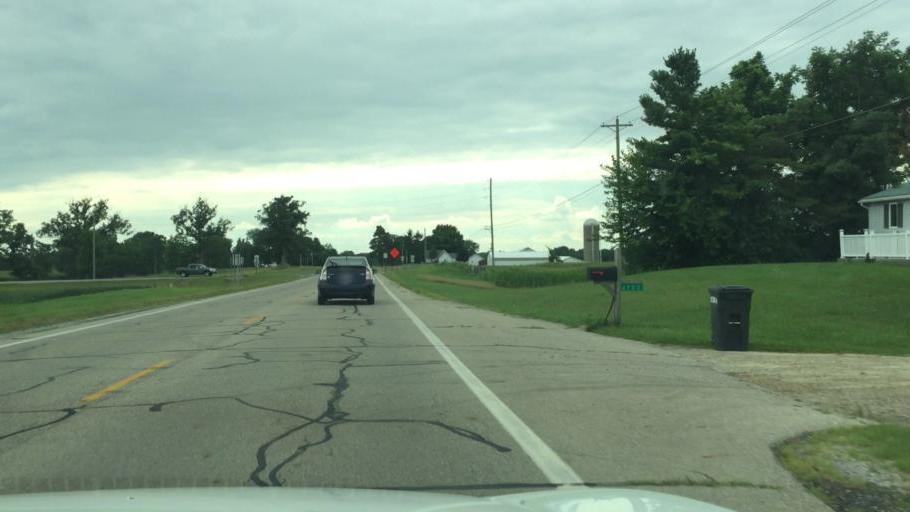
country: US
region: Ohio
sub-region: Champaign County
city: Mechanicsburg
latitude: 40.0785
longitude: -83.6223
